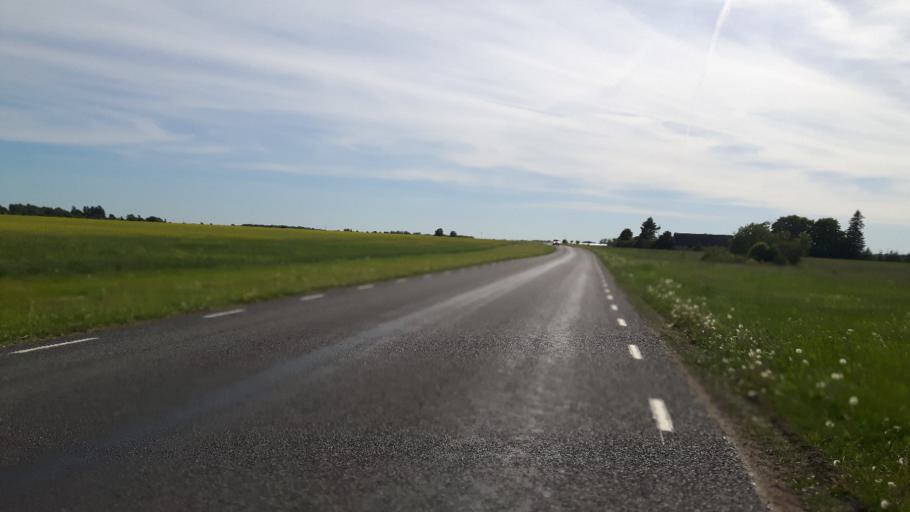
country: EE
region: Harju
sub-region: Raasiku vald
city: Raasiku
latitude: 59.4387
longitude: 25.1297
